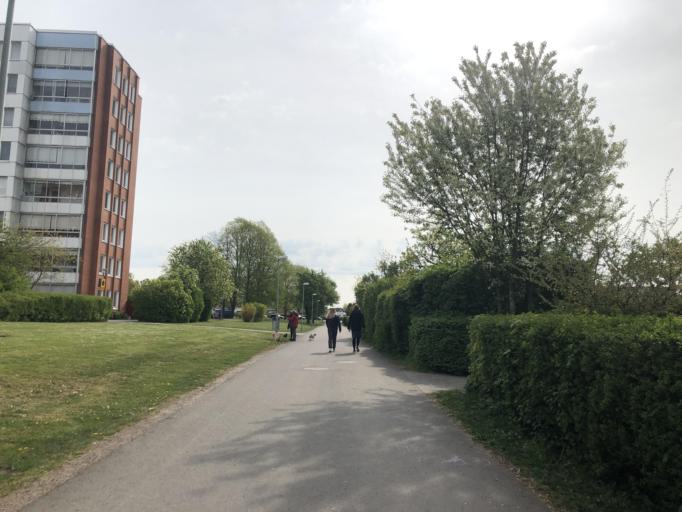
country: SE
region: Skane
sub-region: Landskrona
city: Landskrona
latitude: 55.8810
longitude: 12.8476
